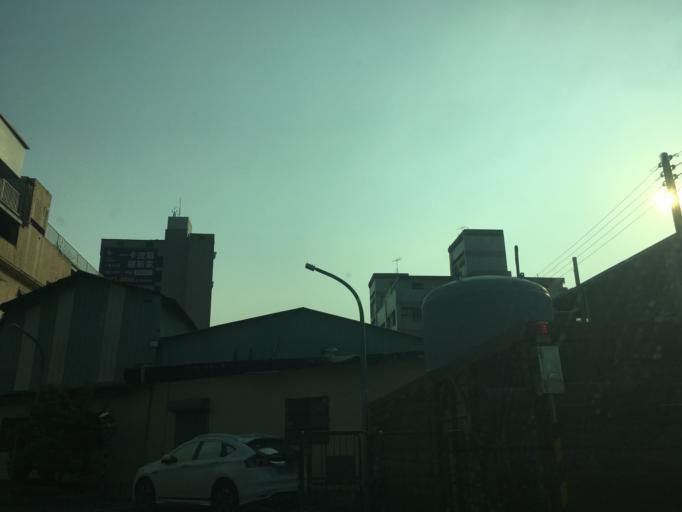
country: TW
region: Taiwan
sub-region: Taichung City
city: Taichung
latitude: 24.1289
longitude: 120.6685
